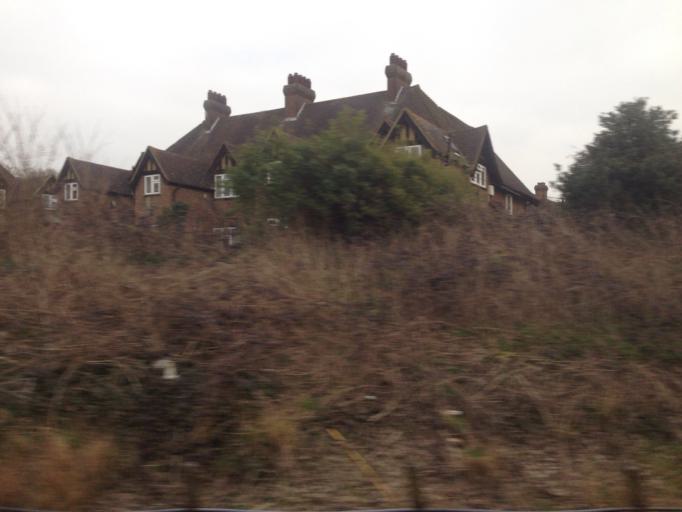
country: GB
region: England
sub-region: Greater London
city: Mitcham
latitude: 51.3959
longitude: -0.1612
